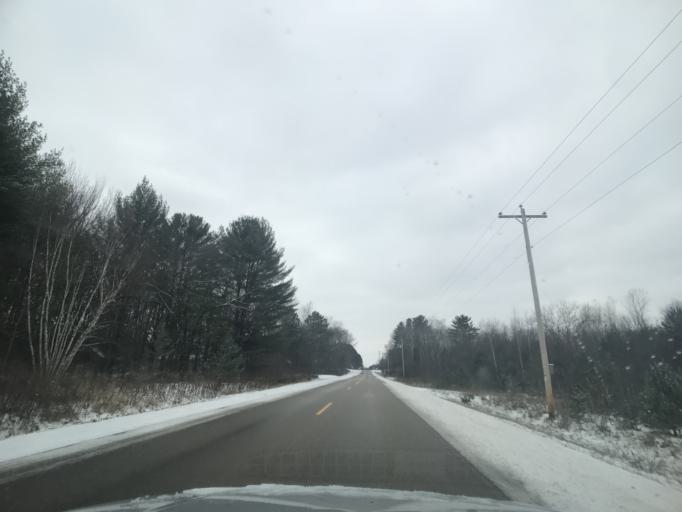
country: US
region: Wisconsin
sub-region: Brown County
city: Suamico
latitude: 44.7063
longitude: -88.0977
